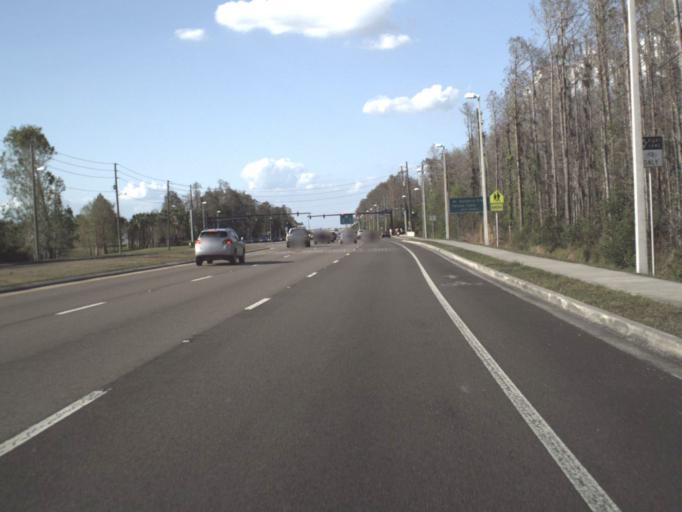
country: US
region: Florida
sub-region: Orange County
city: Hunters Creek
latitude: 28.3597
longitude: -81.4044
